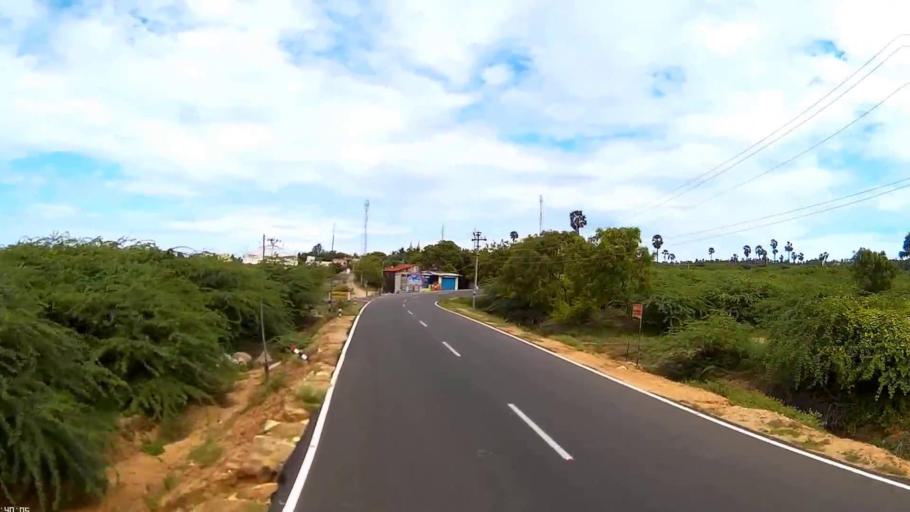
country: IN
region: Tamil Nadu
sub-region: Thoothukkudi
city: Udankudi
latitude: 8.3794
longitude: 78.0505
